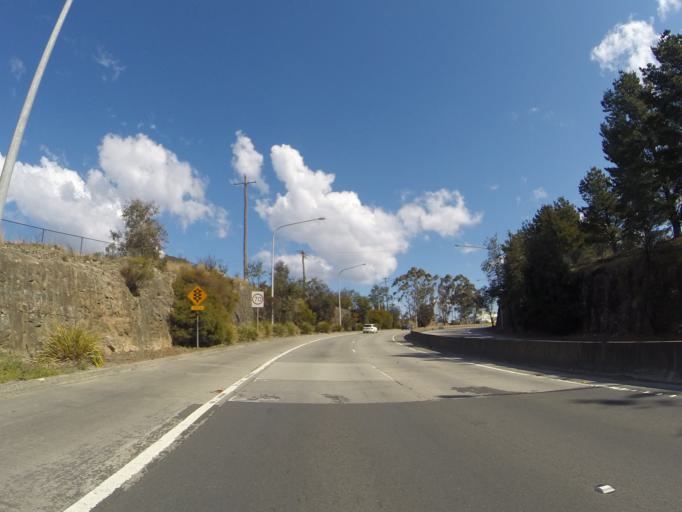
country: AU
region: New South Wales
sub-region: Blue Mountains Municipality
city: Katoomba
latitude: -33.7109
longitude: 150.3151
